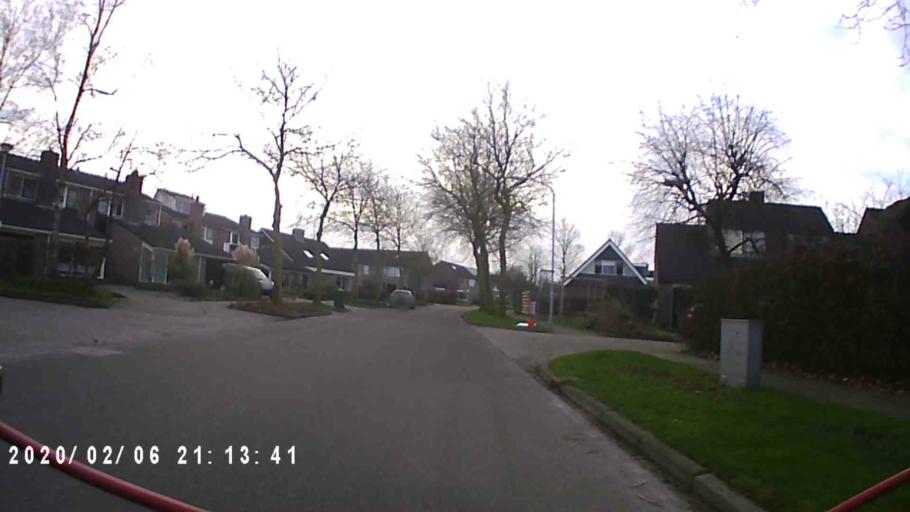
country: NL
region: Groningen
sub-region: Gemeente Zuidhorn
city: Oldehove
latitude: 53.3034
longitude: 6.3904
